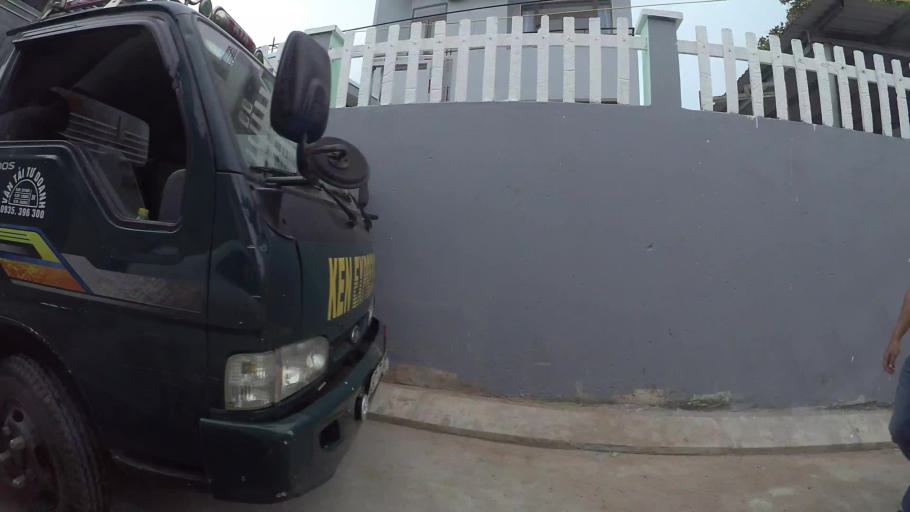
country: VN
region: Da Nang
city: Son Tra
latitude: 16.0832
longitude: 108.2471
